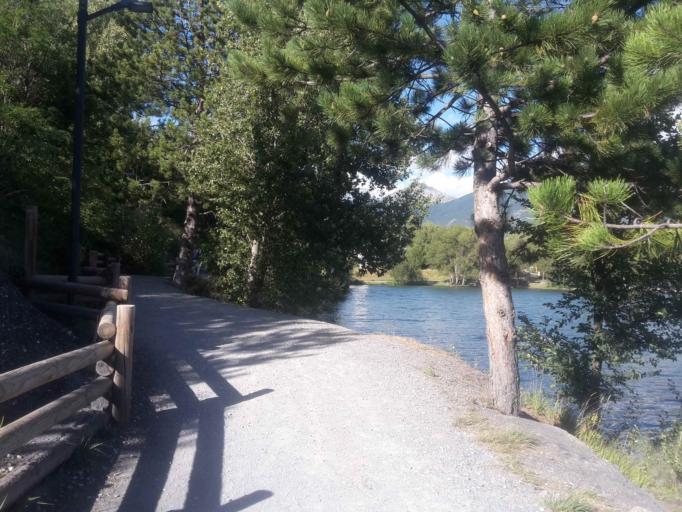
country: FR
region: Provence-Alpes-Cote d'Azur
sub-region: Departement des Hautes-Alpes
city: Embrun
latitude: 44.5503
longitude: 6.4713
